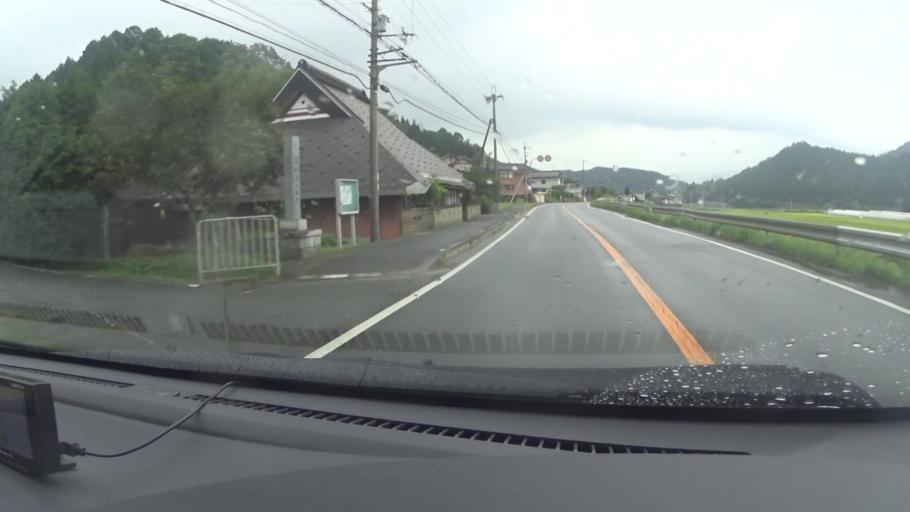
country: JP
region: Kyoto
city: Ayabe
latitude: 35.2024
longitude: 135.3582
